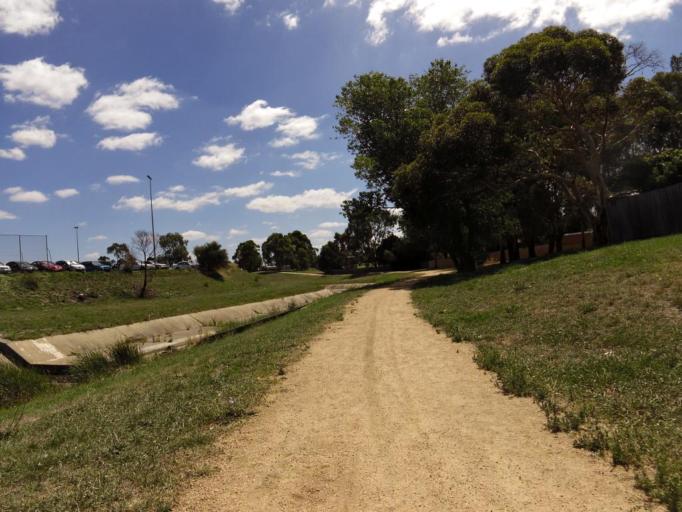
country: AU
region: Victoria
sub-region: Whittlesea
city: Thomastown
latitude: -37.6789
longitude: 145.0077
